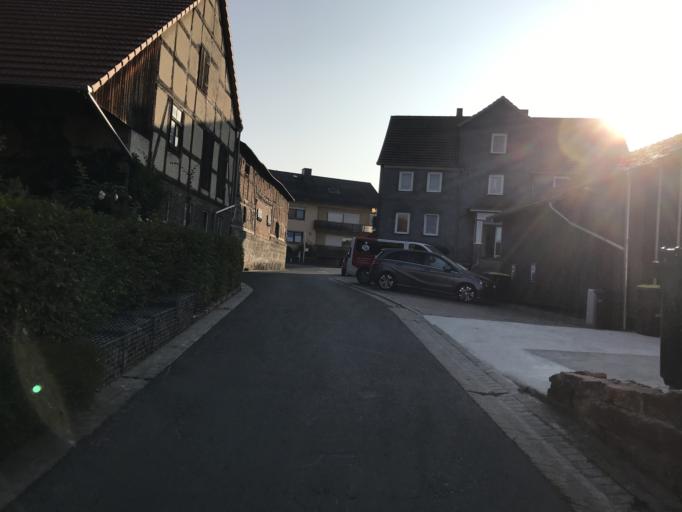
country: DE
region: Hesse
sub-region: Regierungsbezirk Kassel
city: Guxhagen
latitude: 51.2009
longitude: 9.4833
